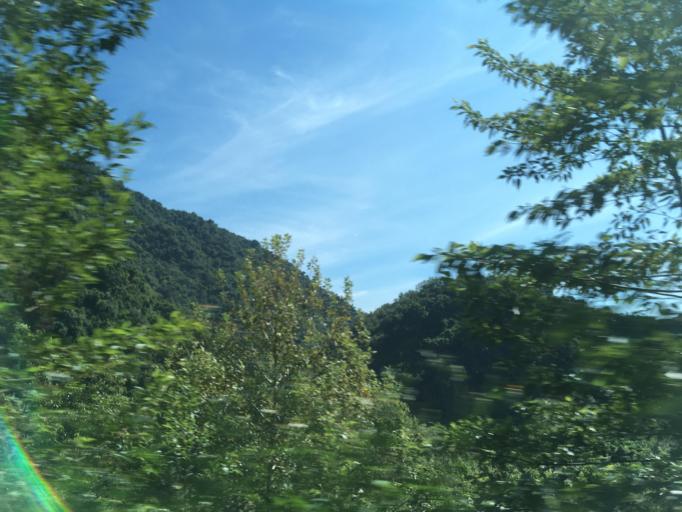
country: TW
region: Taiwan
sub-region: Yilan
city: Yilan
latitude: 24.4197
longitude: 121.7324
